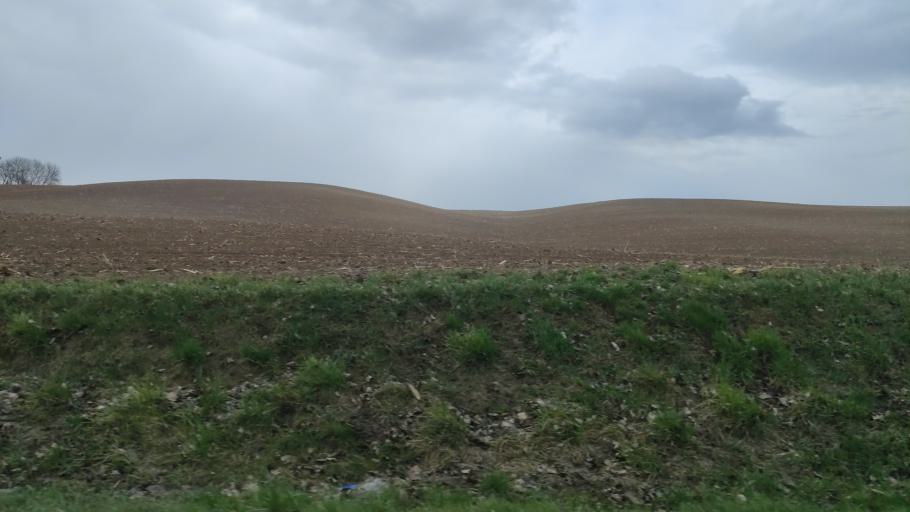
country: PL
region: Kujawsko-Pomorskie
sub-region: Powiat zninski
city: Barcin
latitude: 52.8723
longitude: 17.9001
